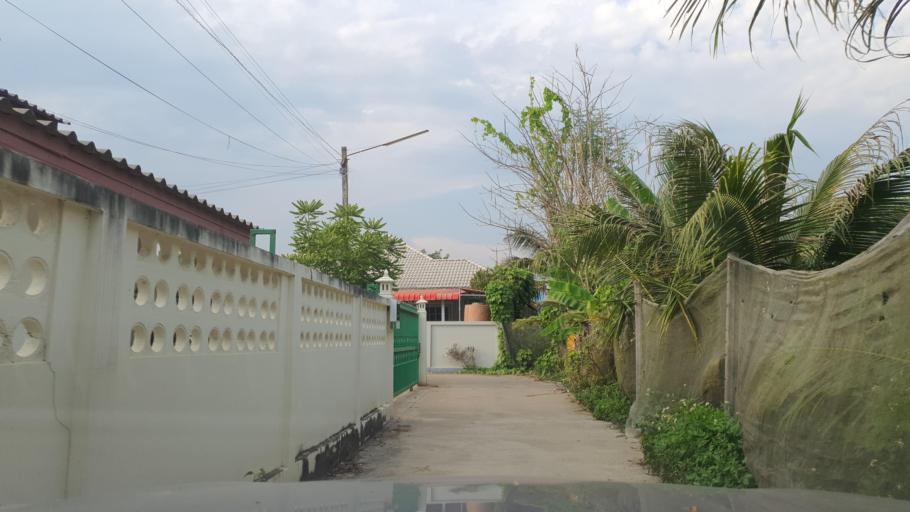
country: TH
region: Chiang Mai
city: Saraphi
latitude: 18.7249
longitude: 98.9917
